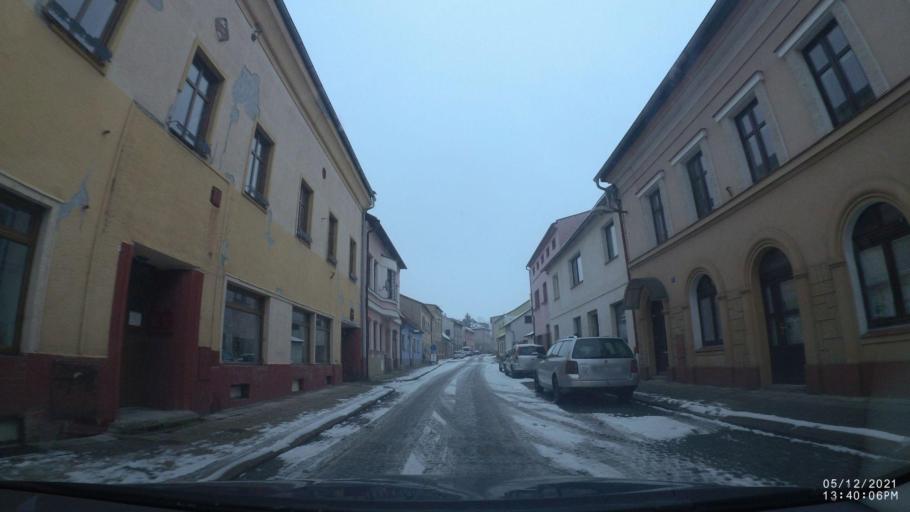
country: CZ
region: Kralovehradecky
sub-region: Okres Nachod
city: Police nad Metuji
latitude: 50.5363
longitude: 16.2350
